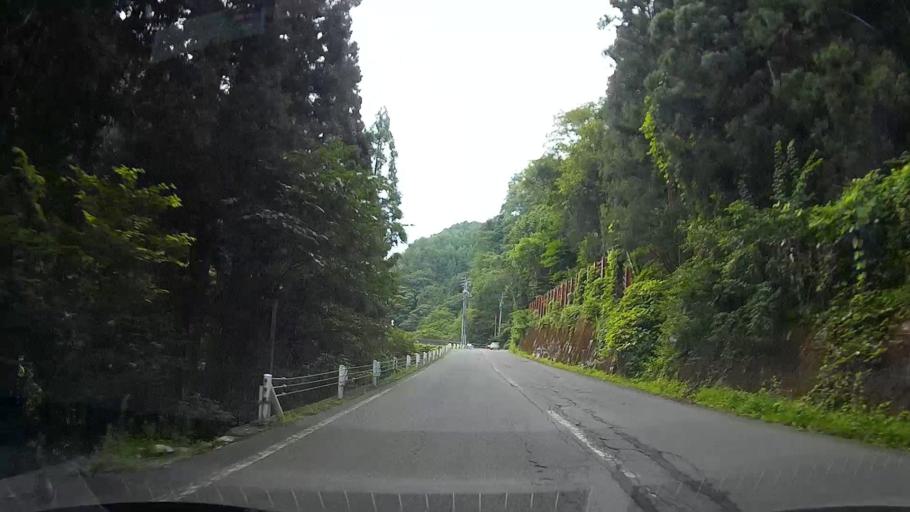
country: JP
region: Nagano
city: Iiyama
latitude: 36.8261
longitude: 138.4251
